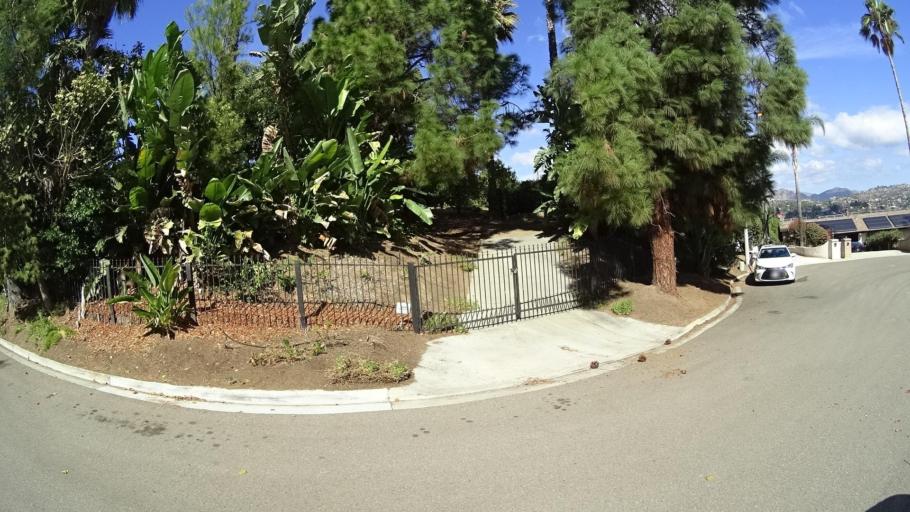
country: US
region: California
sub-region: San Diego County
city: Rancho San Diego
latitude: 32.7664
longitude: -116.9333
